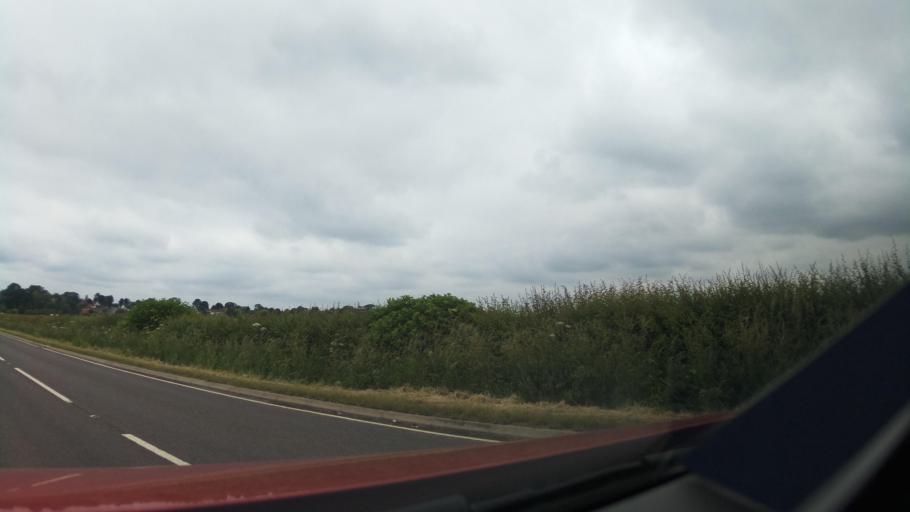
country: GB
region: England
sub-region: Leicestershire
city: Melton Mowbray
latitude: 52.7369
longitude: -0.8556
